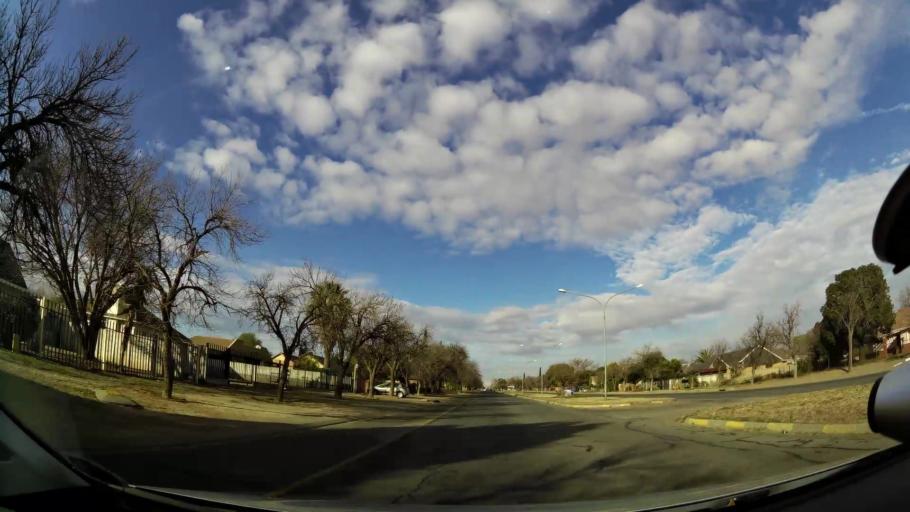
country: ZA
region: Orange Free State
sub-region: Lejweleputswa District Municipality
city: Welkom
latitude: -27.9824
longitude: 26.7214
